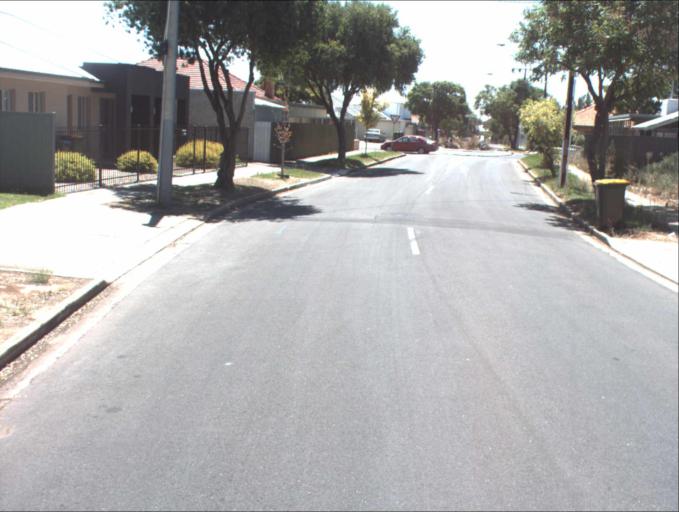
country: AU
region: South Australia
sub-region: Port Adelaide Enfield
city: Blair Athol
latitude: -34.8680
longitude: 138.6122
